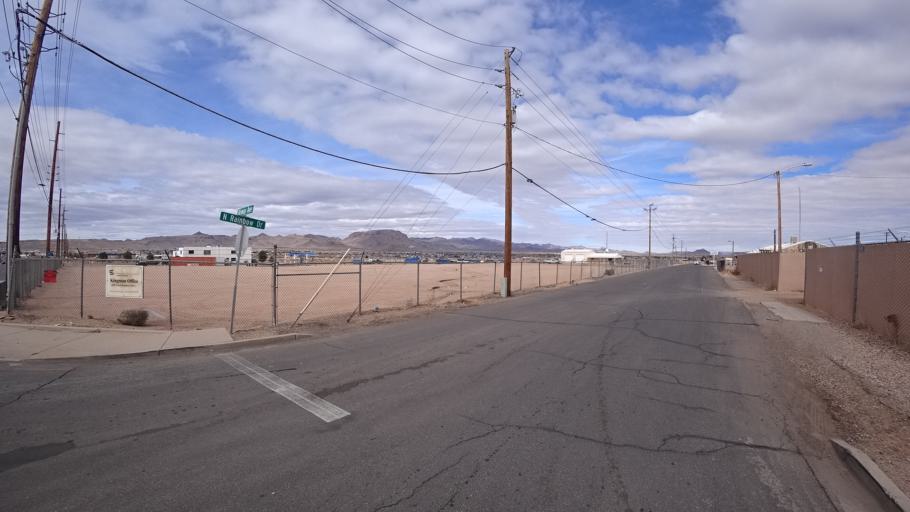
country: US
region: Arizona
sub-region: Mohave County
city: New Kingman-Butler
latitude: 35.2250
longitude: -114.0056
